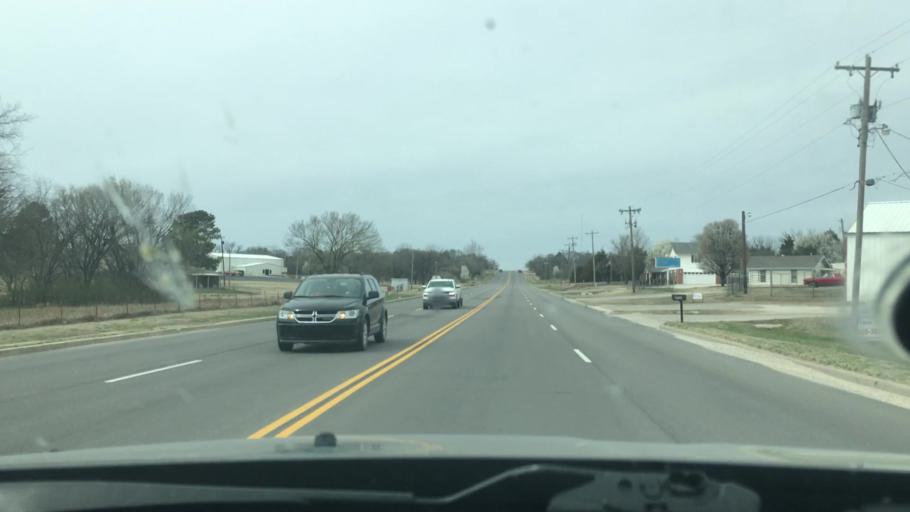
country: US
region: Oklahoma
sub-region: Seminole County
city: Seminole
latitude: 35.2513
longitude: -96.7046
